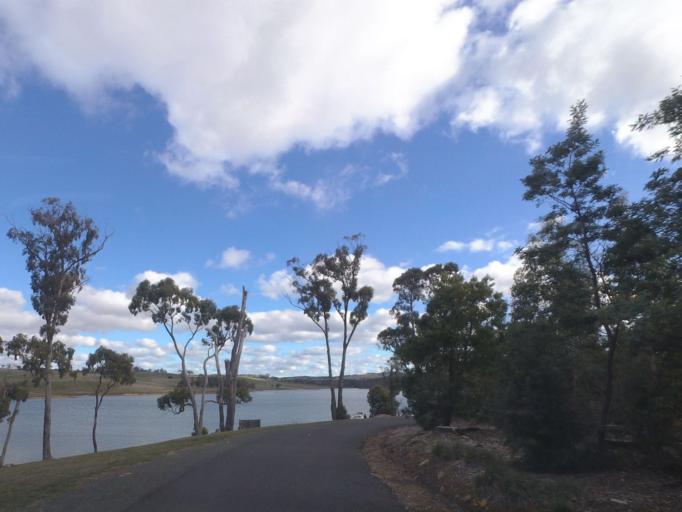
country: AU
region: Victoria
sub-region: Mount Alexander
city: Castlemaine
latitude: -37.2557
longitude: 144.3823
